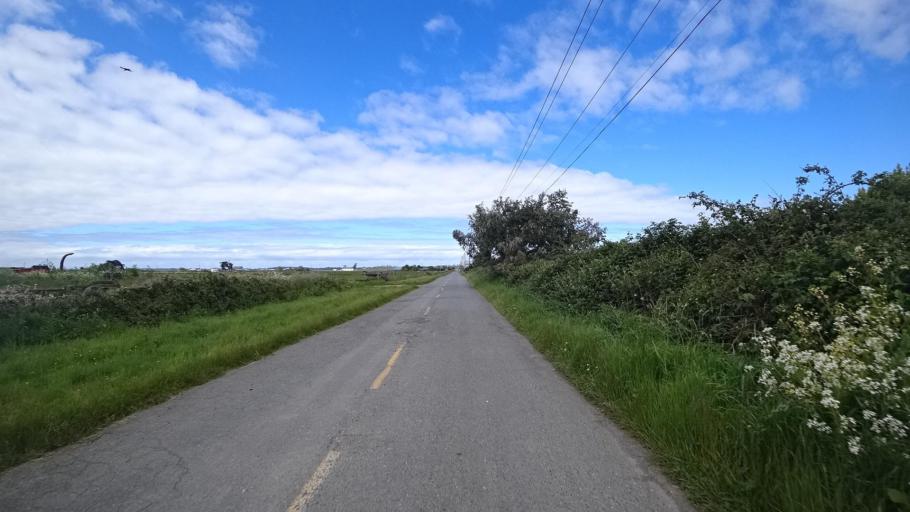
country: US
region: California
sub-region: Humboldt County
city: Arcata
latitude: 40.8831
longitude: -124.1093
